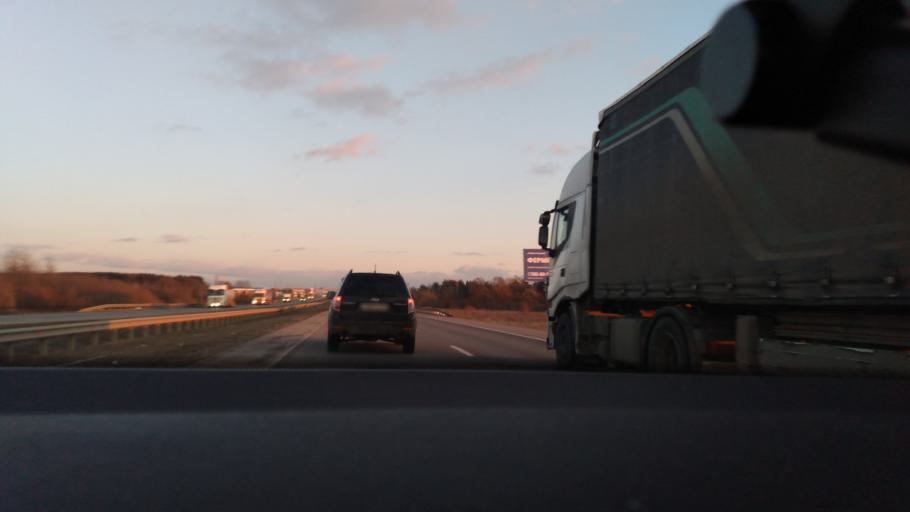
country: RU
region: Moskovskaya
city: Kolomna
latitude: 55.1248
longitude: 38.7990
